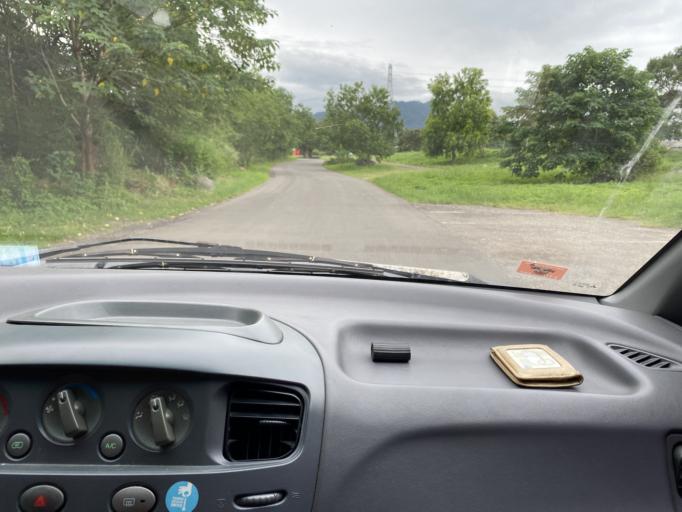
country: TW
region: Taiwan
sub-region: Hsinchu
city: Zhubei
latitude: 24.7213
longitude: 121.1031
